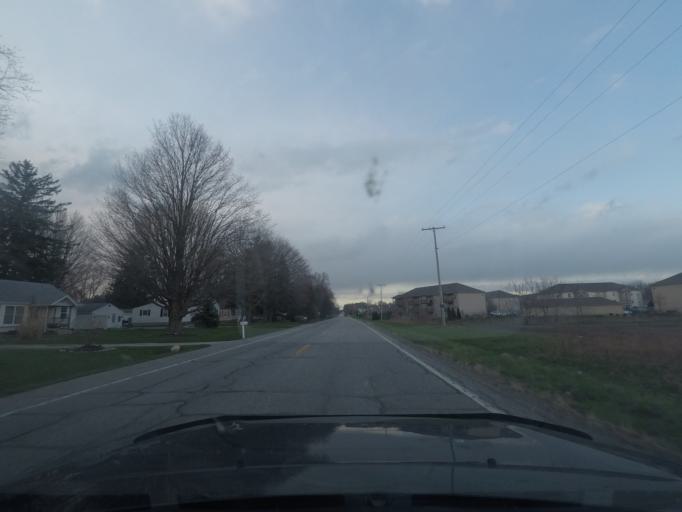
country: US
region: Indiana
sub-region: LaPorte County
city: LaPorte
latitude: 41.5870
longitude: -86.7391
